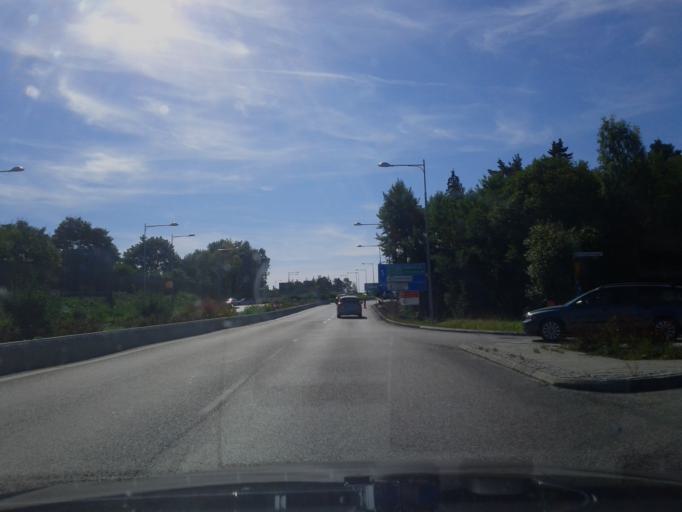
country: SE
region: Stockholm
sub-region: Taby Kommun
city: Taby
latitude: 59.4461
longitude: 18.0951
